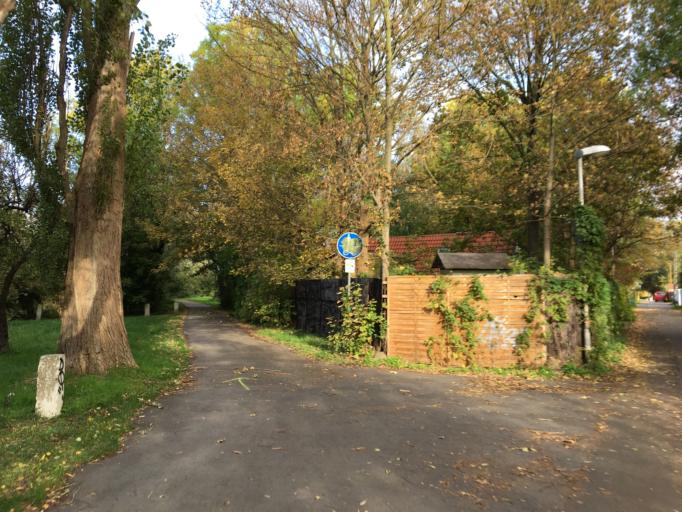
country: DE
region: Lower Saxony
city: Braunschweig
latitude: 52.2856
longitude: 10.5130
